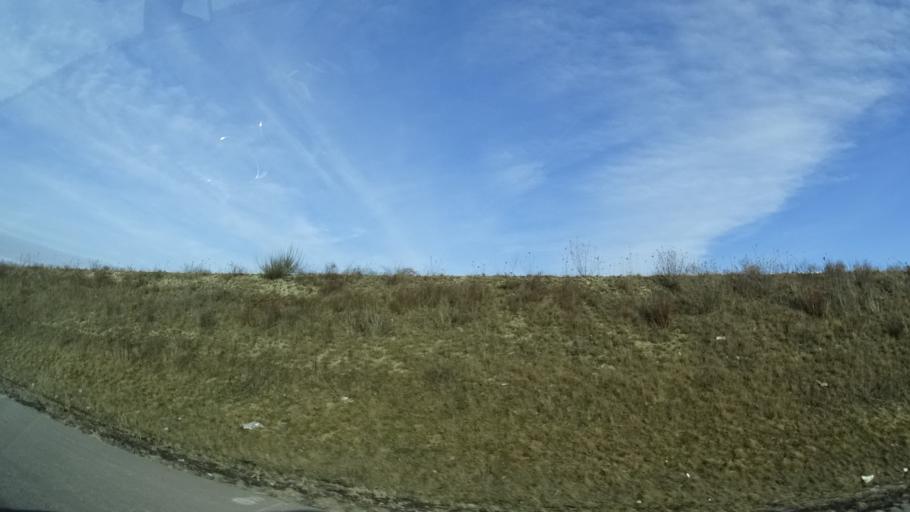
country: DE
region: Thuringia
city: Bucha
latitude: 50.8843
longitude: 11.4828
